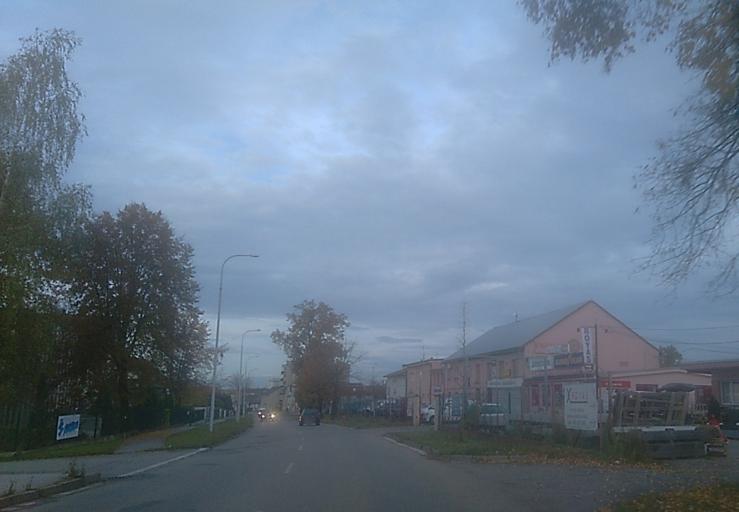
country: CZ
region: Jihocesky
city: Rudolfov
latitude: 48.9714
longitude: 14.5121
